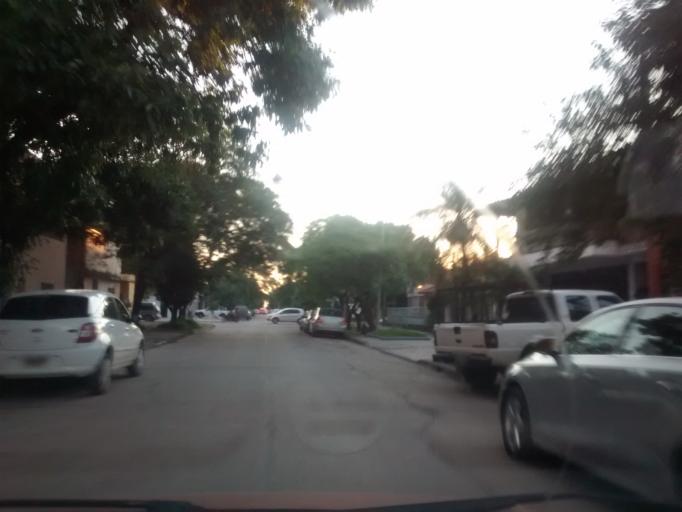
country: AR
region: Chaco
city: Resistencia
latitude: -27.4538
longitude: -58.9947
